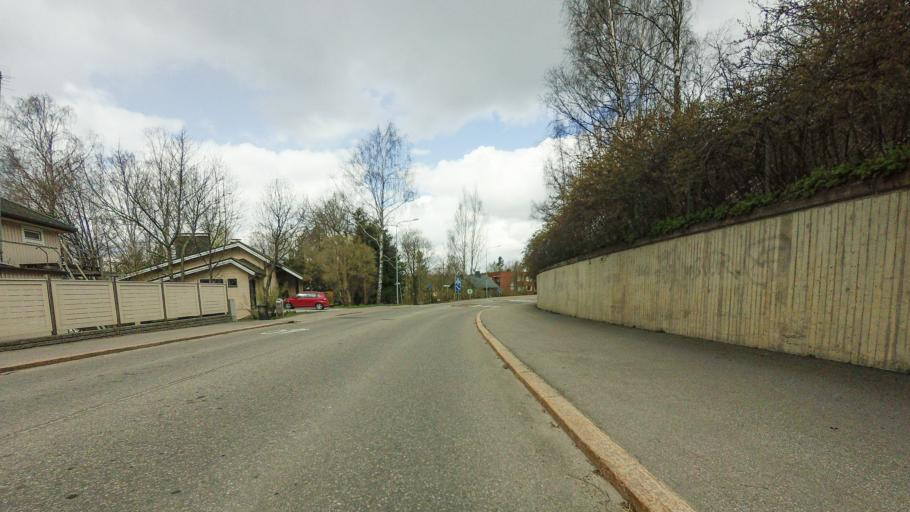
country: FI
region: Uusimaa
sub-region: Helsinki
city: Vantaa
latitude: 60.2217
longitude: 25.0938
